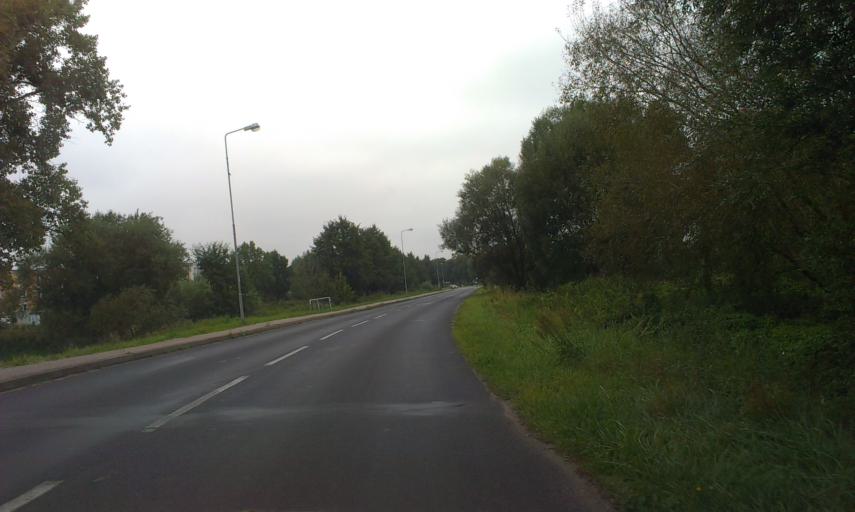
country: PL
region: West Pomeranian Voivodeship
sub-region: Powiat szczecinecki
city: Barwice
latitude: 53.7388
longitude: 16.3524
